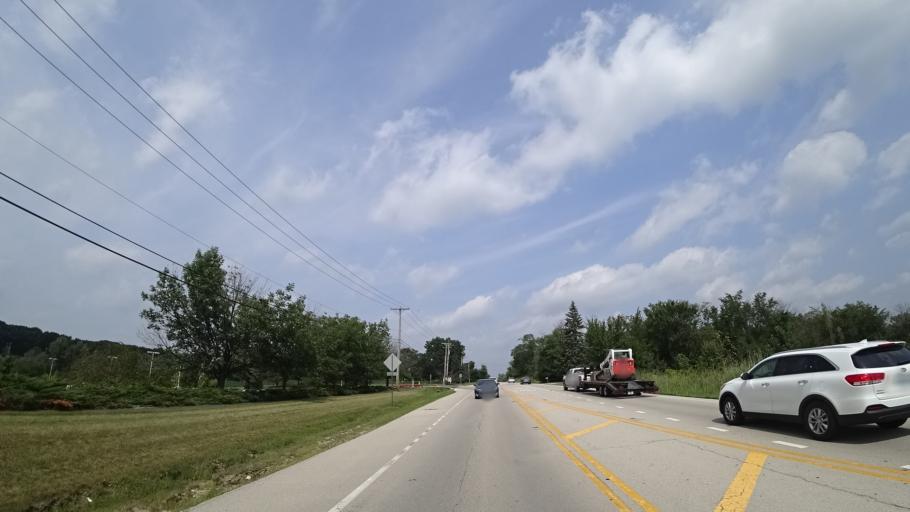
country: US
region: Illinois
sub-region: Cook County
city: Orland Park
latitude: 41.6168
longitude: -87.8920
